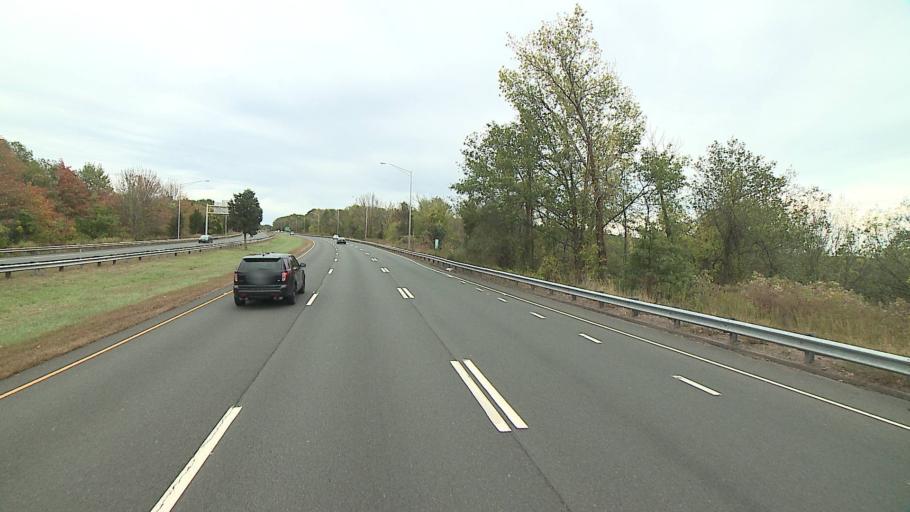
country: US
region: Connecticut
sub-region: Middlesex County
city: Middletown
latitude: 41.5304
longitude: -72.6166
